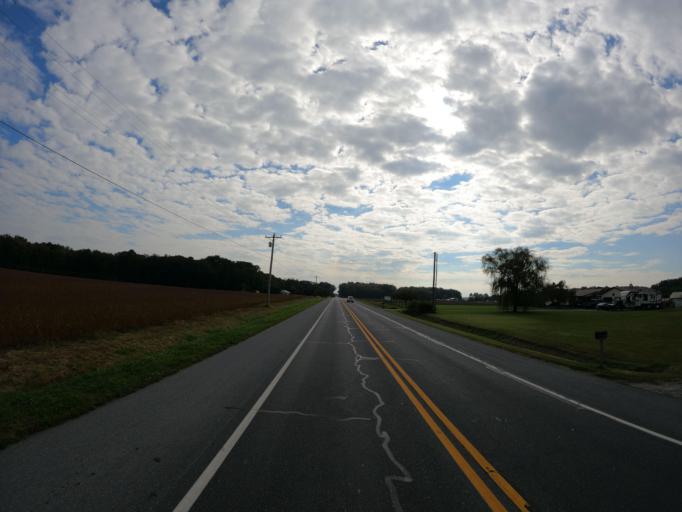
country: US
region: Delaware
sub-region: Sussex County
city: Bridgeville
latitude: 38.7674
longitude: -75.6481
